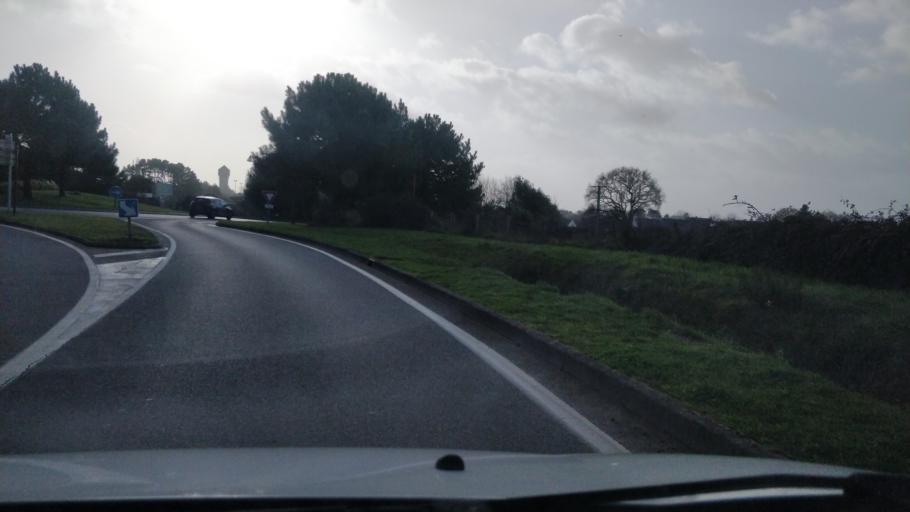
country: FR
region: Pays de la Loire
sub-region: Departement de la Loire-Atlantique
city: Guerande
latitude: 47.3419
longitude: -2.4283
